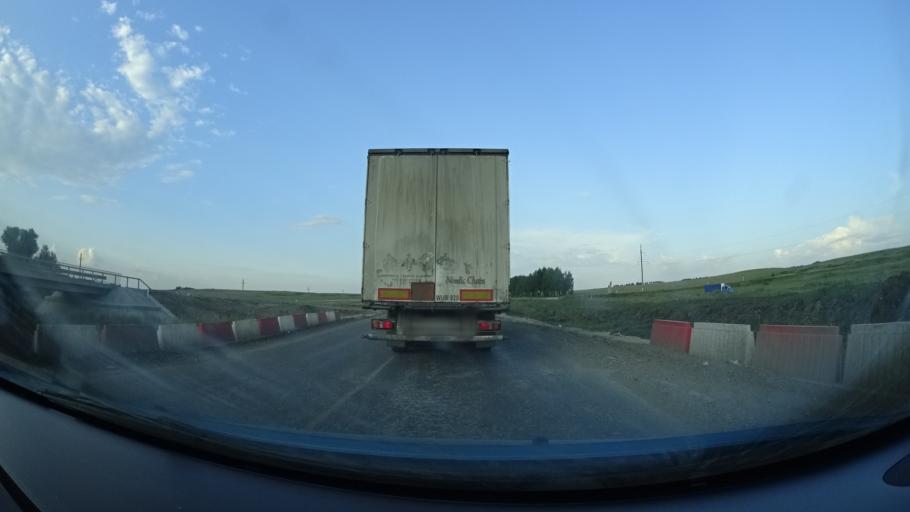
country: RU
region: Samara
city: Kamyshla
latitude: 54.0474
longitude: 52.0182
